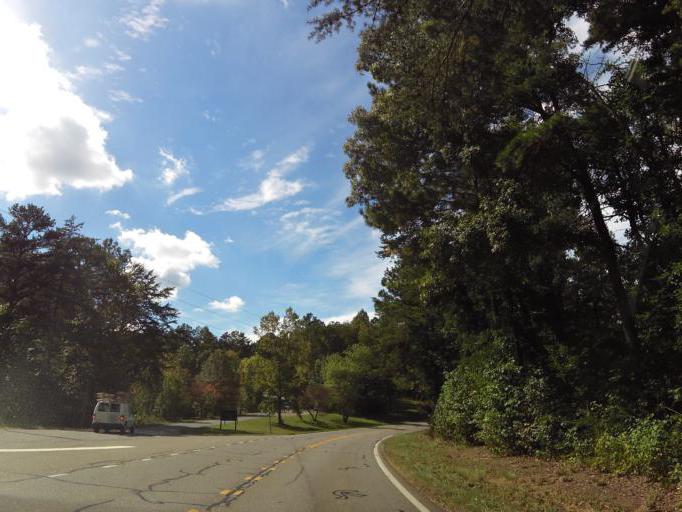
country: US
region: Georgia
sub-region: Pickens County
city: Nelson
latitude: 34.4125
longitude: -84.2933
